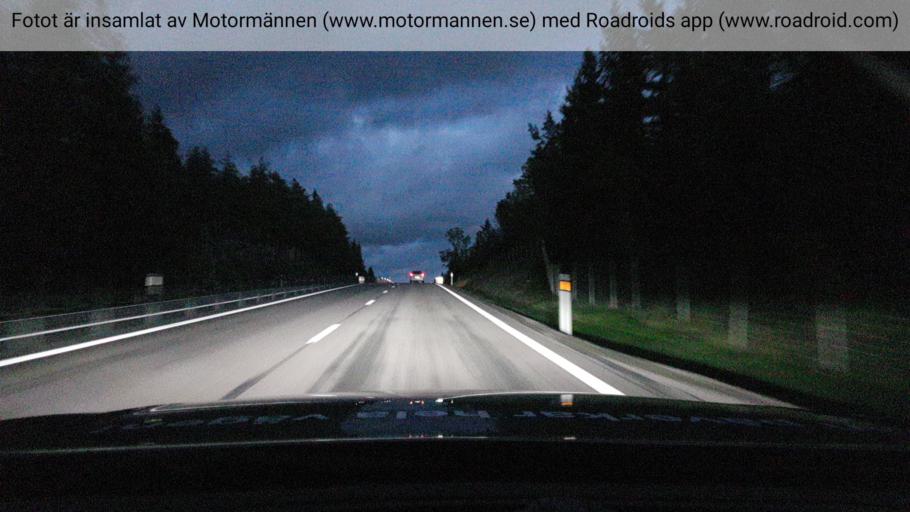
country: SE
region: Vaermland
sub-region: Kristinehamns Kommun
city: Kristinehamn
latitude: 59.3123
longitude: 14.1803
